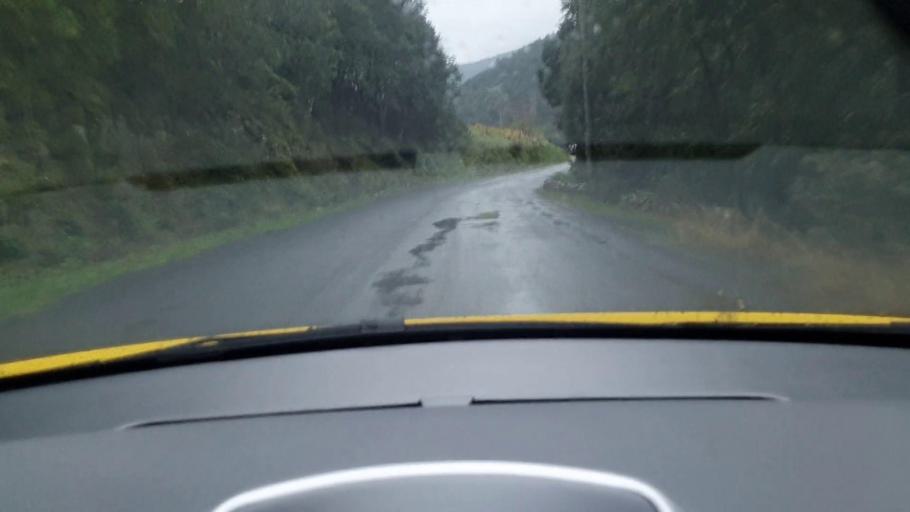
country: FR
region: Languedoc-Roussillon
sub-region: Departement du Gard
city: Sumene
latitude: 44.0166
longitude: 3.7226
